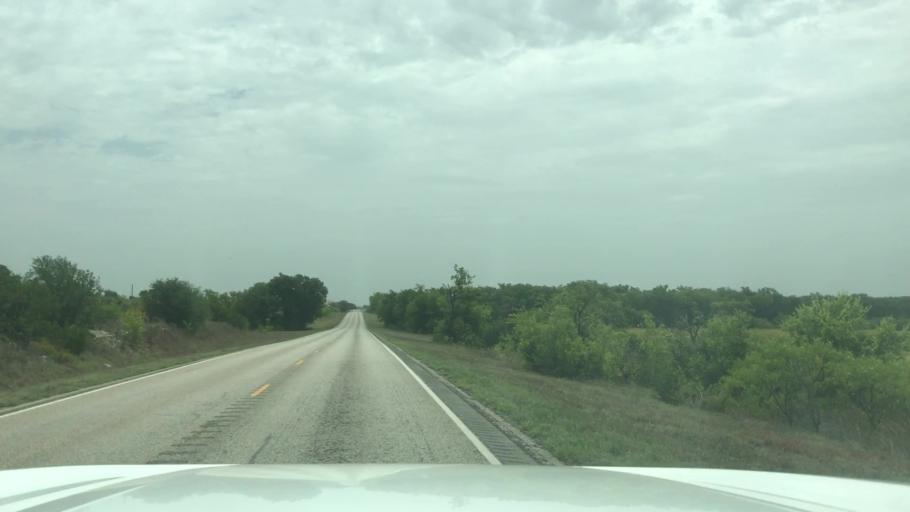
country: US
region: Texas
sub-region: Hamilton County
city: Hico
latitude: 32.0493
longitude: -98.1578
